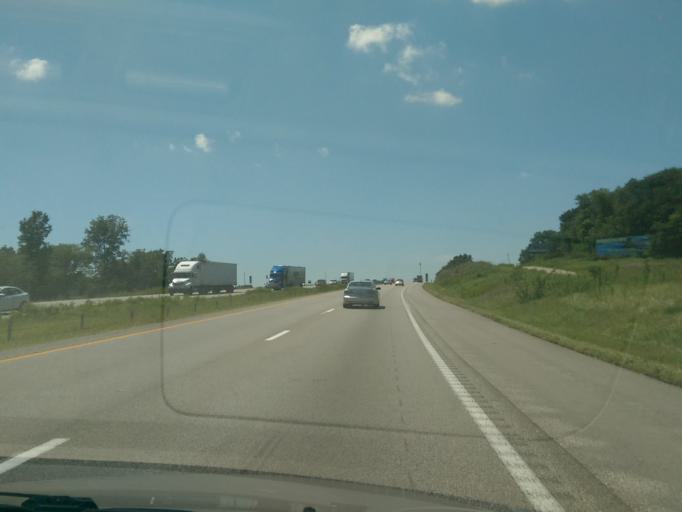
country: US
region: Missouri
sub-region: Saline County
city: Marshall
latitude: 38.9703
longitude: -93.2490
